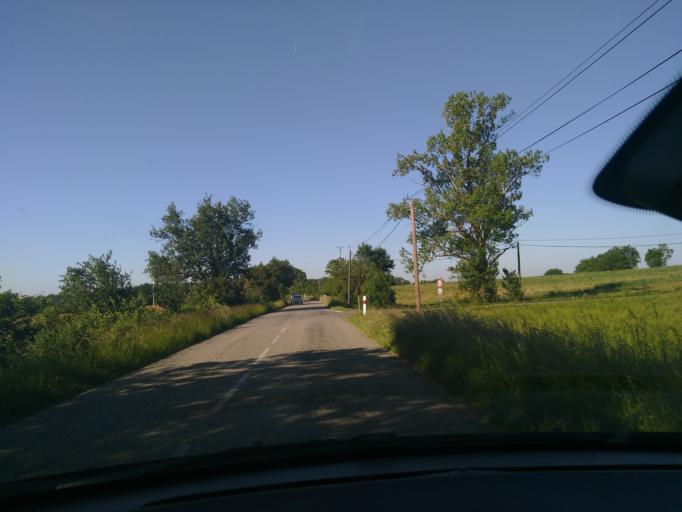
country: FR
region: Midi-Pyrenees
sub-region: Departement du Gers
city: Gimont
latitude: 43.6991
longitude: 0.8764
